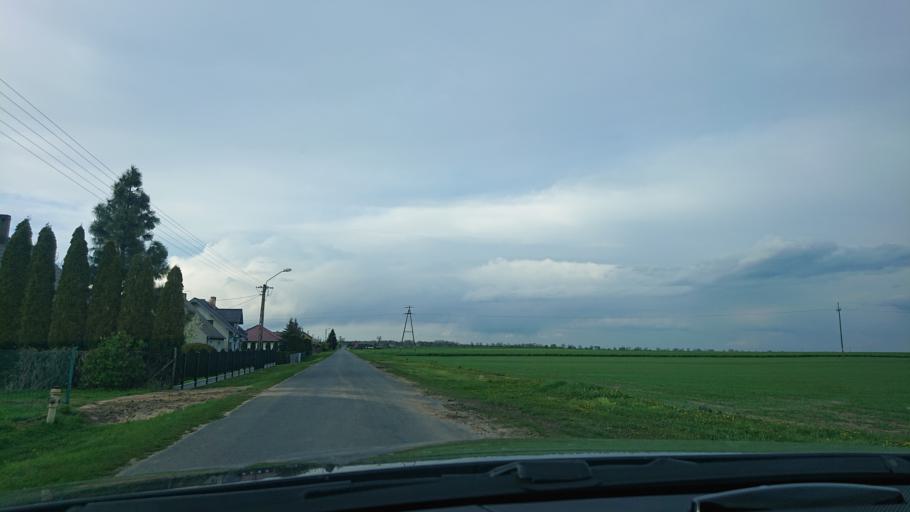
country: PL
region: Greater Poland Voivodeship
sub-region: Powiat gnieznienski
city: Lubowo
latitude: 52.5731
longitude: 17.4762
